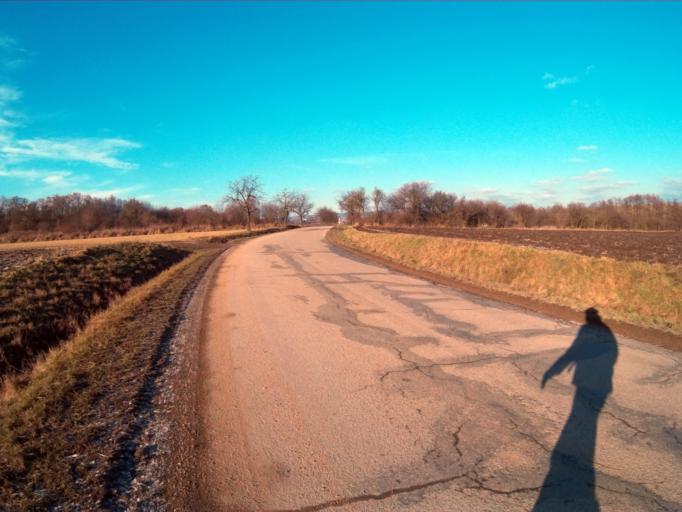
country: CZ
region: South Moravian
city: Krenovice
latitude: 49.1531
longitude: 16.8210
